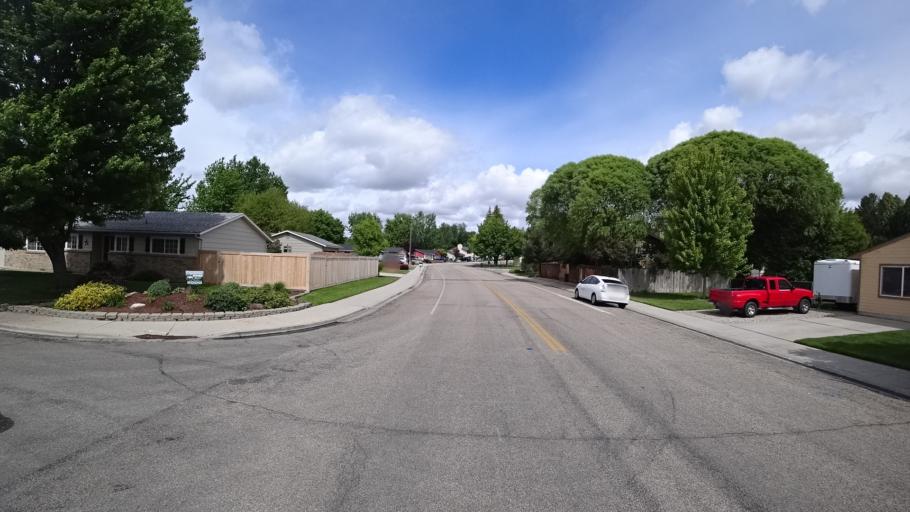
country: US
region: Idaho
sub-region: Ada County
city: Eagle
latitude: 43.6975
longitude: -116.3486
